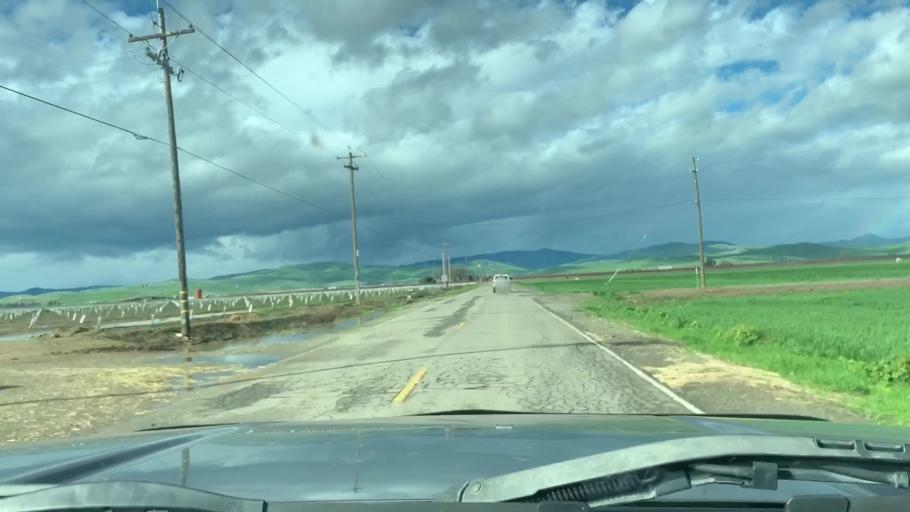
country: US
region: California
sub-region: Merced County
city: Gustine
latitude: 37.1224
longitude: -121.0024
